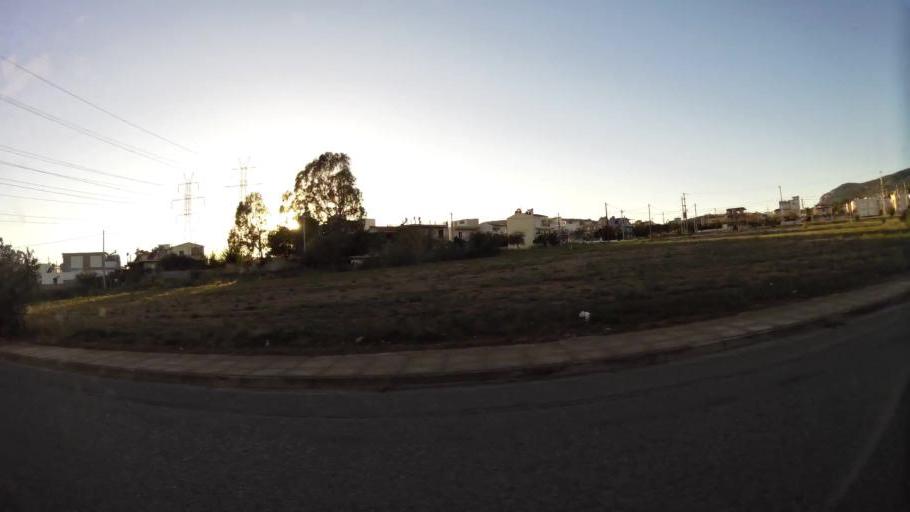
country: GR
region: Attica
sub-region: Nomarchia Dytikis Attikis
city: Ano Liosia
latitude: 38.0915
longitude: 23.7001
